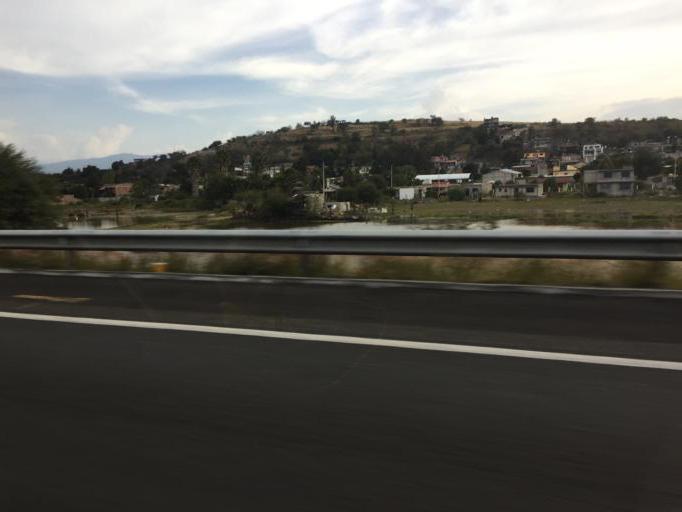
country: MX
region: Michoacan
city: Querendaro
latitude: 19.8846
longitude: -100.9458
